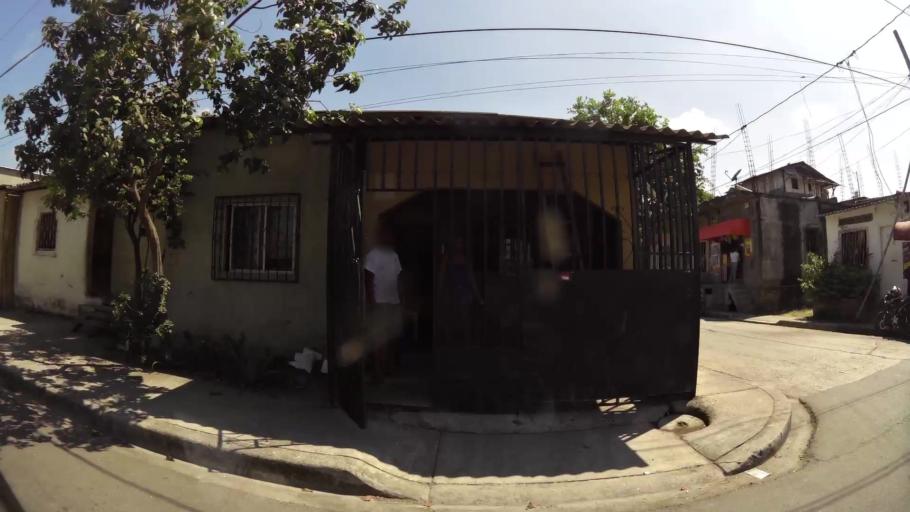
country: EC
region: Guayas
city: Guayaquil
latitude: -2.1301
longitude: -79.9265
